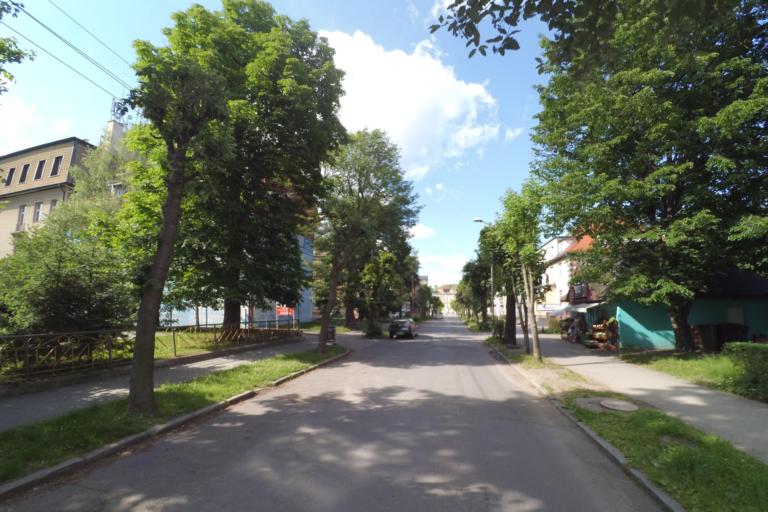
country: PL
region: Lower Silesian Voivodeship
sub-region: Powiat klodzki
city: Klodzko
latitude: 50.4340
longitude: 16.6512
